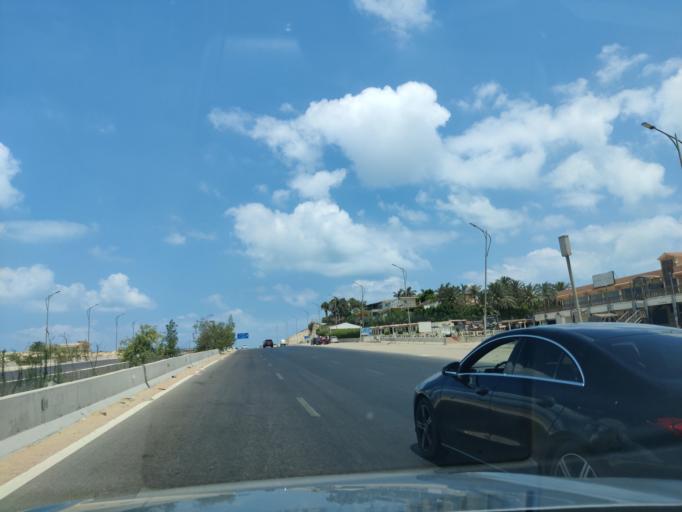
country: EG
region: Alexandria
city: Alexandria
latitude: 31.0097
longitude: 29.6370
